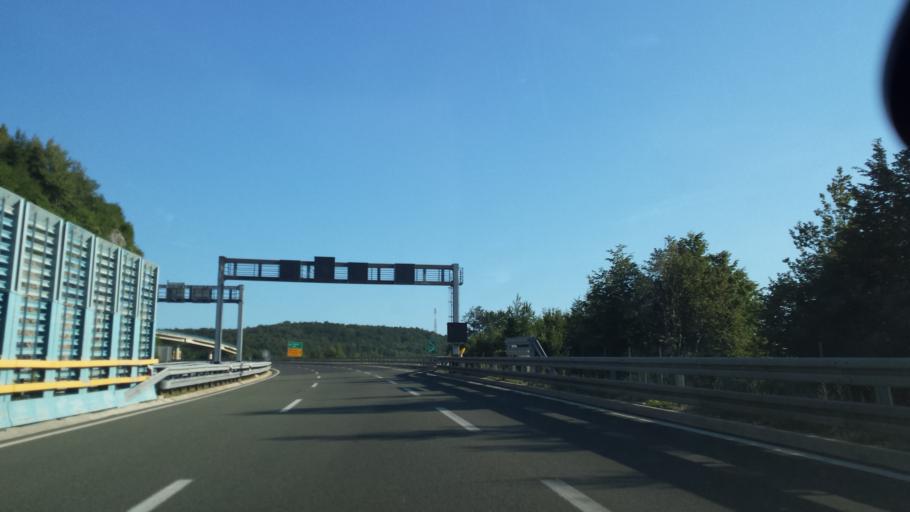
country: HR
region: Primorsko-Goranska
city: Krasica
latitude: 45.3420
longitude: 14.5935
